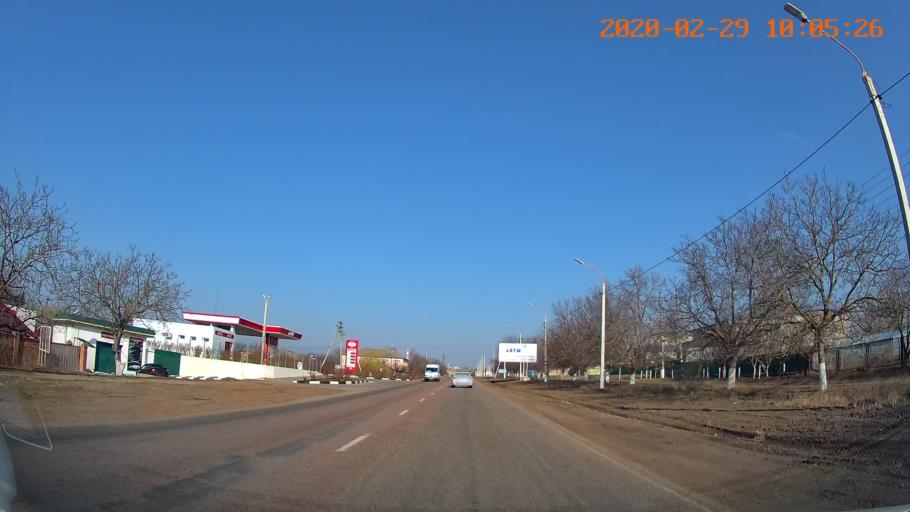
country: MD
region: Telenesti
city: Tiraspolul Nou
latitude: 46.8071
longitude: 29.6714
